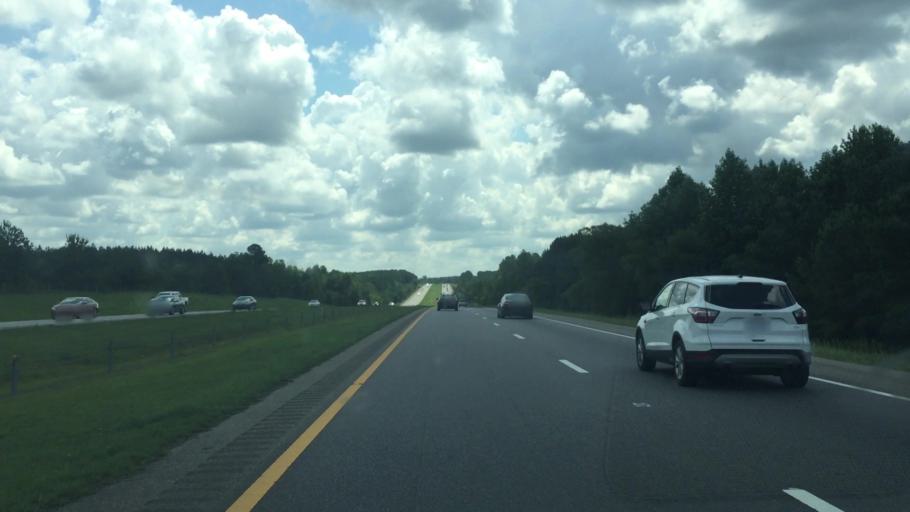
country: US
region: North Carolina
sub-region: Richmond County
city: East Rockingham
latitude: 34.8821
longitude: -79.7819
